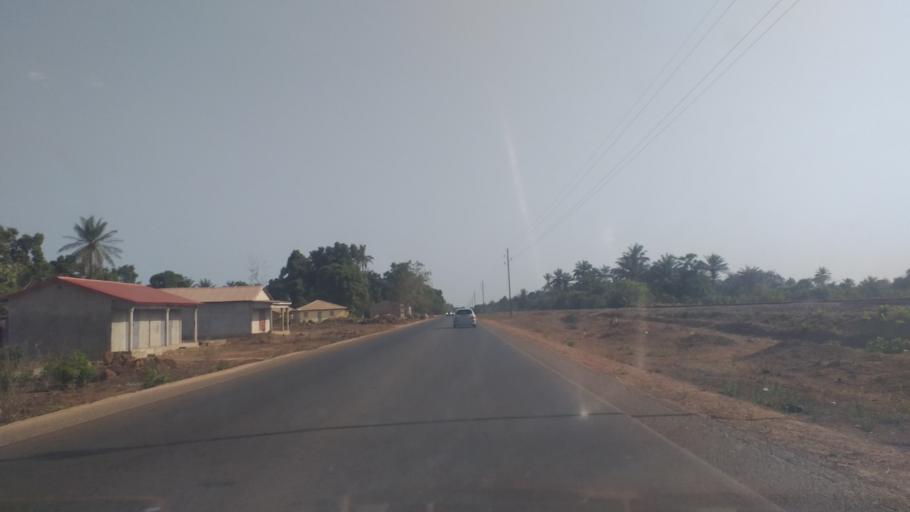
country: GN
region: Boke
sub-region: Boke Prefecture
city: Kamsar
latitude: 10.7226
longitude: -14.5200
